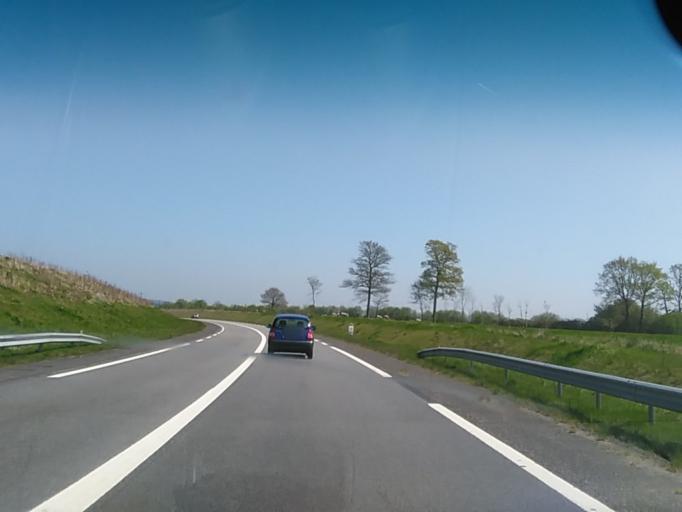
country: FR
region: Lower Normandy
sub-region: Departement de l'Orne
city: Aube-sur-Rile
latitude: 48.7265
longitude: 0.4988
